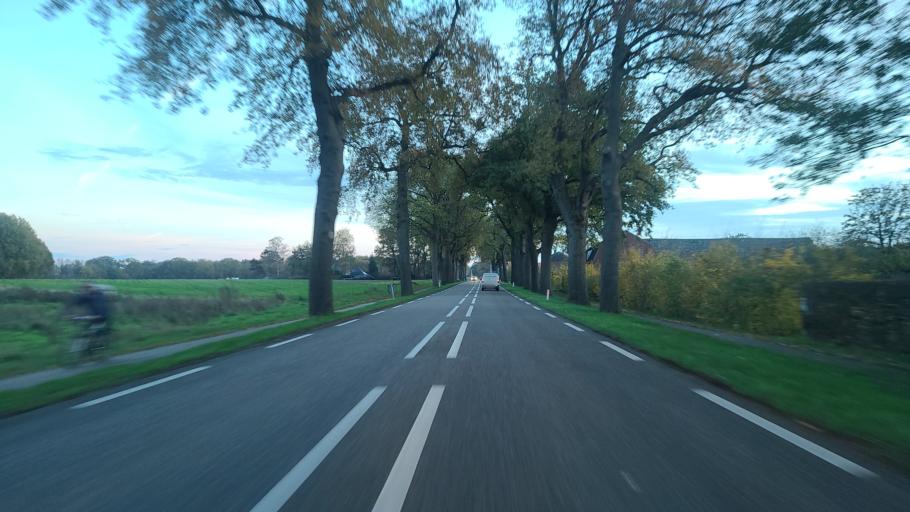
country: NL
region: Limburg
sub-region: Gemeente Bergen
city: Wellerlooi
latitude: 51.5925
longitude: 6.0589
